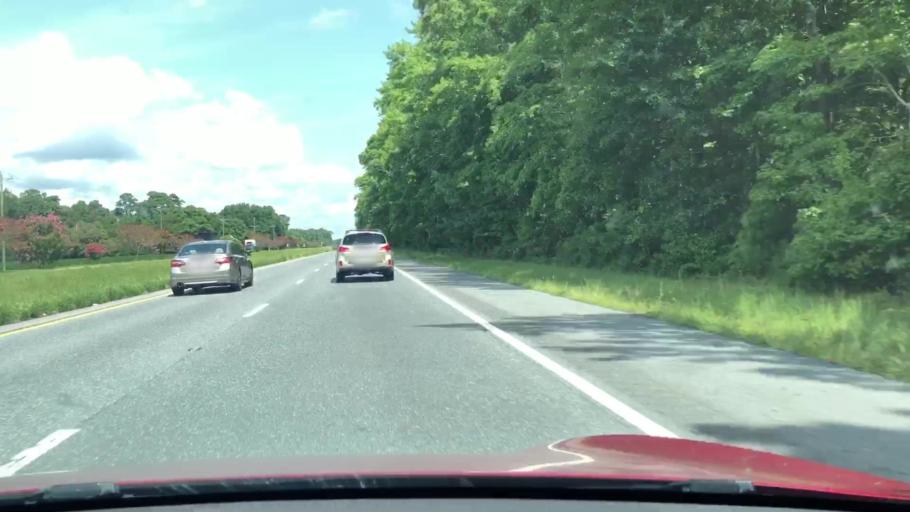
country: US
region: Virginia
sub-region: Northampton County
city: Eastville
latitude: 37.3077
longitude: -75.9636
